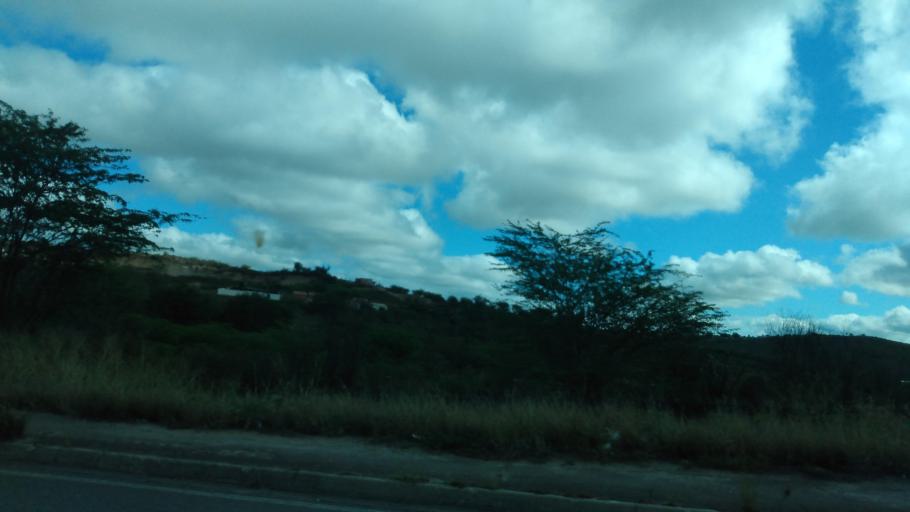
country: BR
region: Pernambuco
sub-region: Caruaru
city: Caruaru
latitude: -8.3088
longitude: -36.0265
